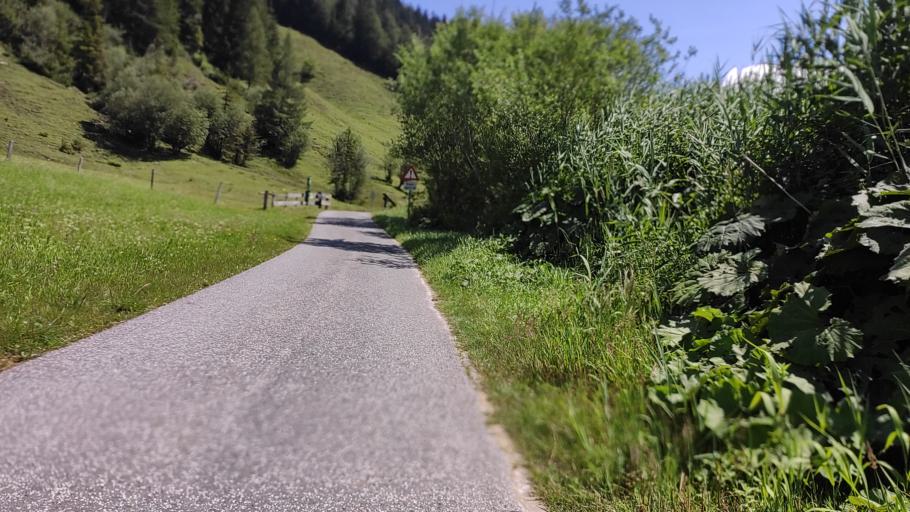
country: AT
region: Tyrol
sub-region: Politischer Bezirk Kitzbuhel
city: Hochfilzen
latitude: 47.4637
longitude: 12.6409
